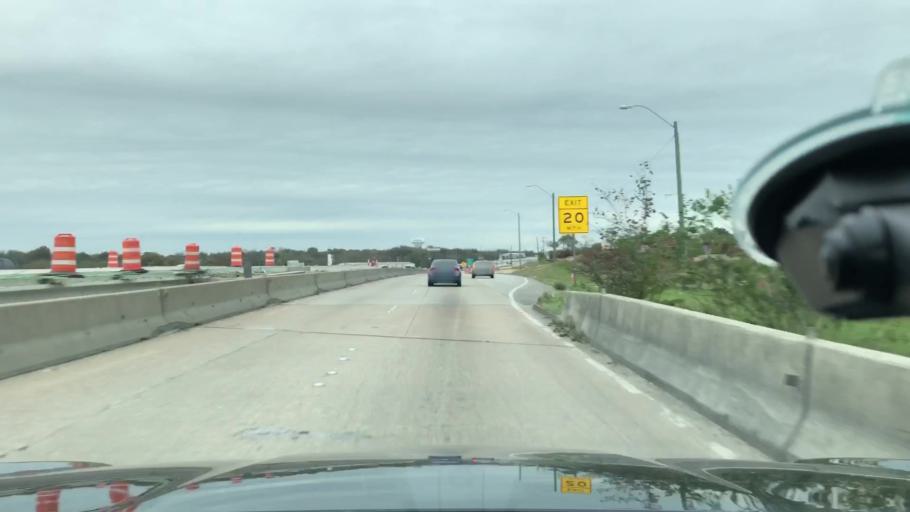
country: US
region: Texas
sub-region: Ellis County
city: Waxahachie
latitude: 32.4083
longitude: -96.8727
